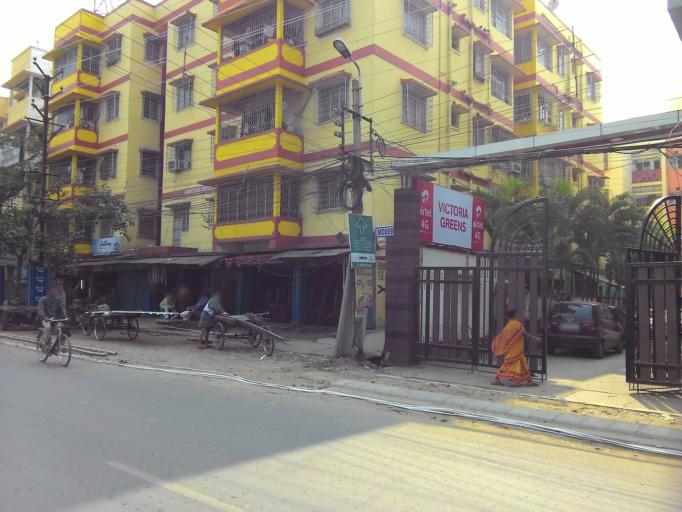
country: IN
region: West Bengal
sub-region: Kolkata
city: Kolkata
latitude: 22.4588
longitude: 88.3831
